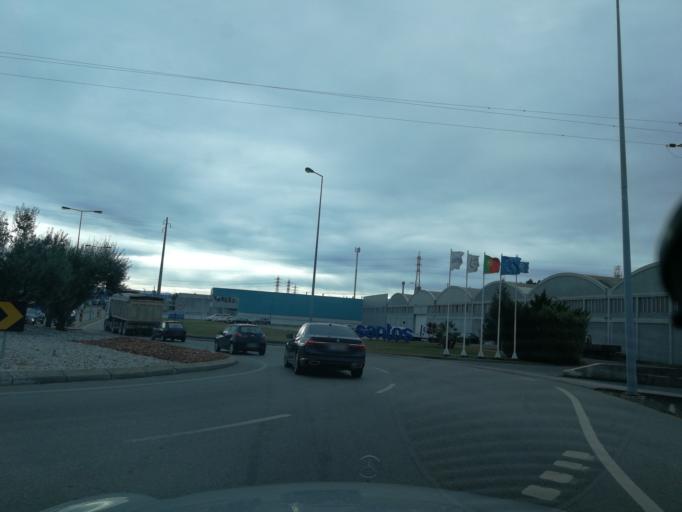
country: PT
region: Aveiro
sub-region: Agueda
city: Valongo
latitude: 40.5951
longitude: -8.4662
